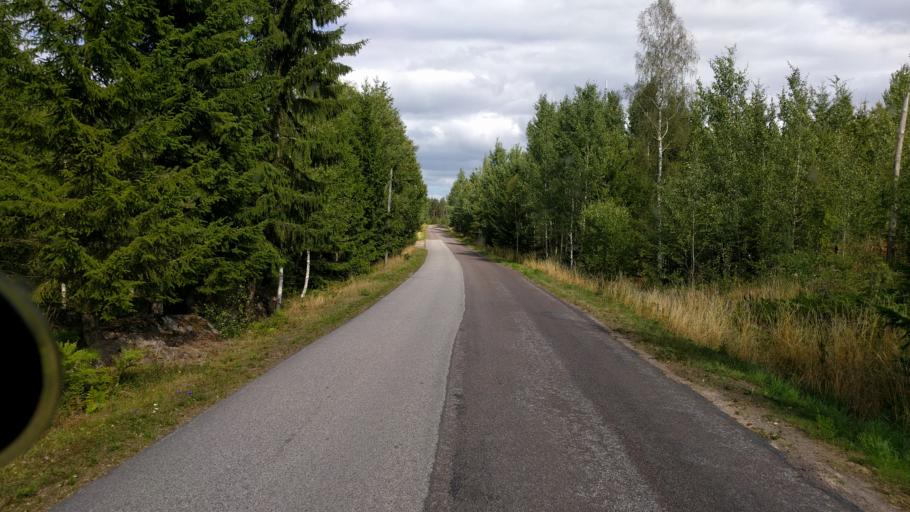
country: SE
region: Kalmar
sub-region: Vimmerby Kommun
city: Vimmerby
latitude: 57.7084
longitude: 16.0215
